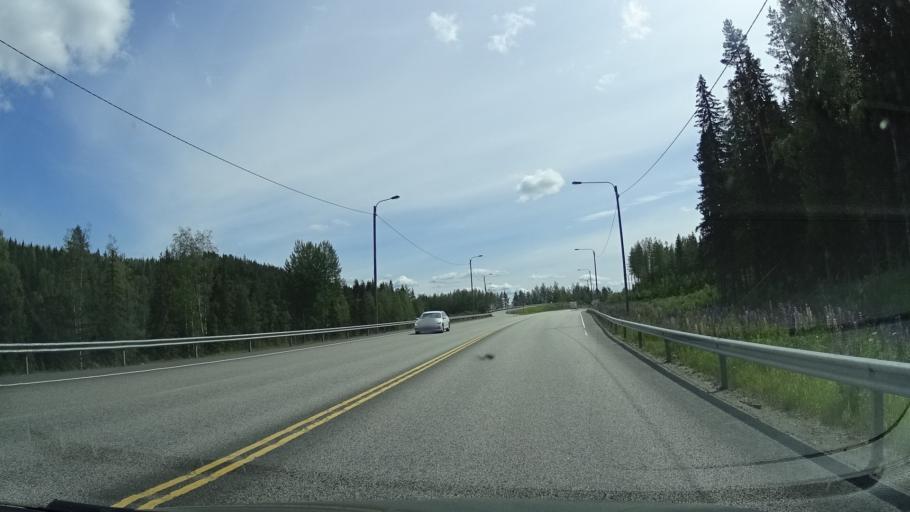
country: FI
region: Central Finland
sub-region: Jyvaeskylae
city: Jyvaeskylae
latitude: 62.2515
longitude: 25.6436
